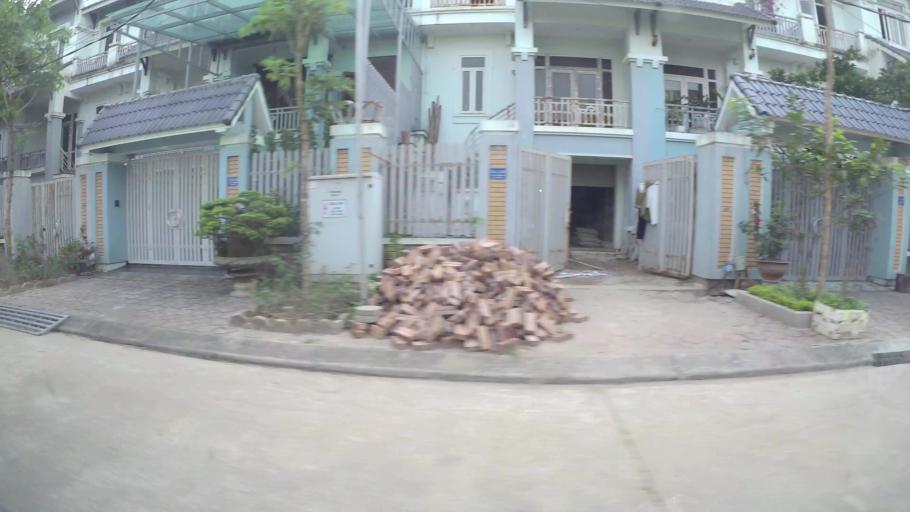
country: VN
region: Ha Noi
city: Cau Dien
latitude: 21.0088
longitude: 105.7328
